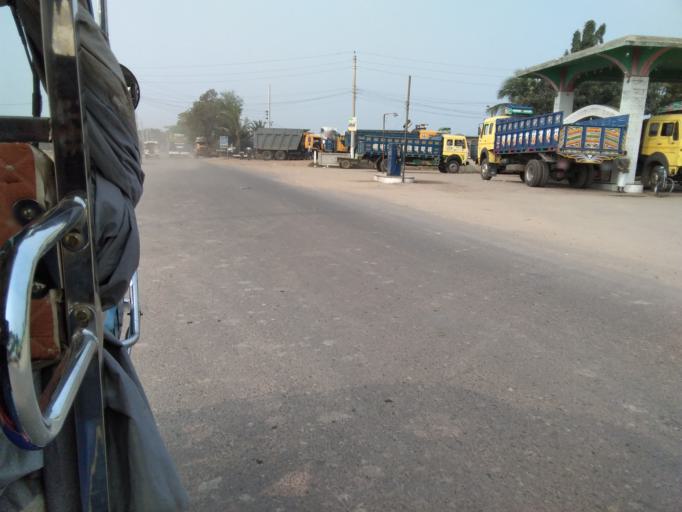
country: BD
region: Khulna
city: Satkhira
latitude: 22.6905
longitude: 89.0412
